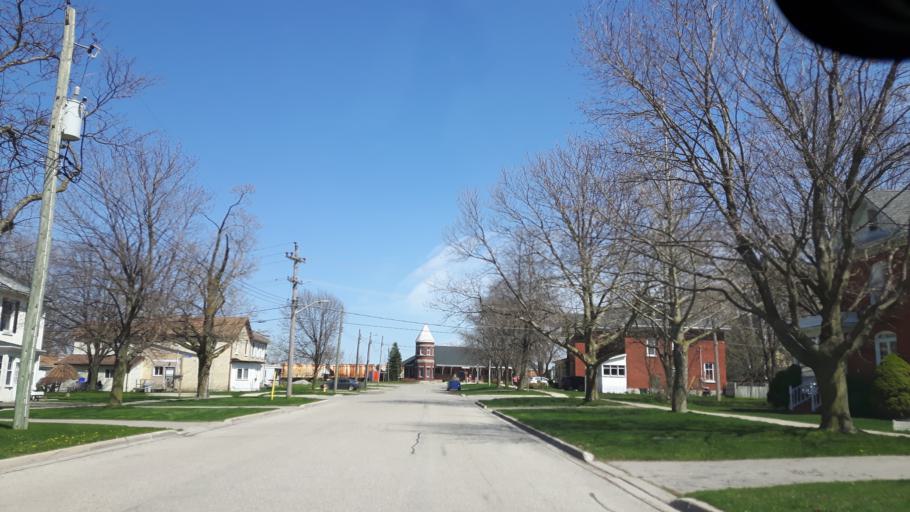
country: CA
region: Ontario
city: Goderich
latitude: 43.7431
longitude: -81.7022
